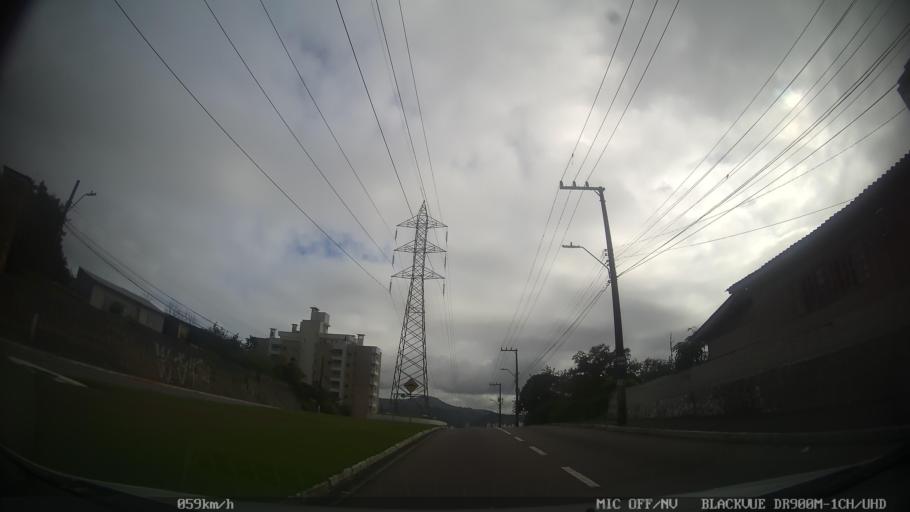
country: BR
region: Santa Catarina
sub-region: Sao Jose
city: Campinas
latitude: -27.5724
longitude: -48.6279
